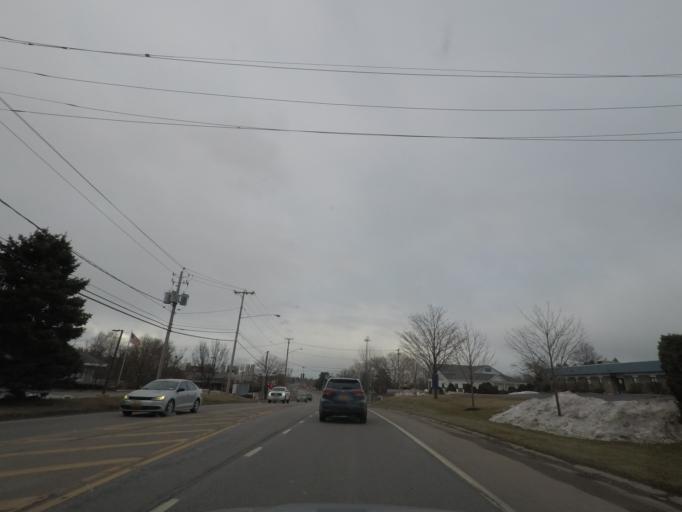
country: US
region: New York
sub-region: Madison County
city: Oneida
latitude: 43.0786
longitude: -75.6532
